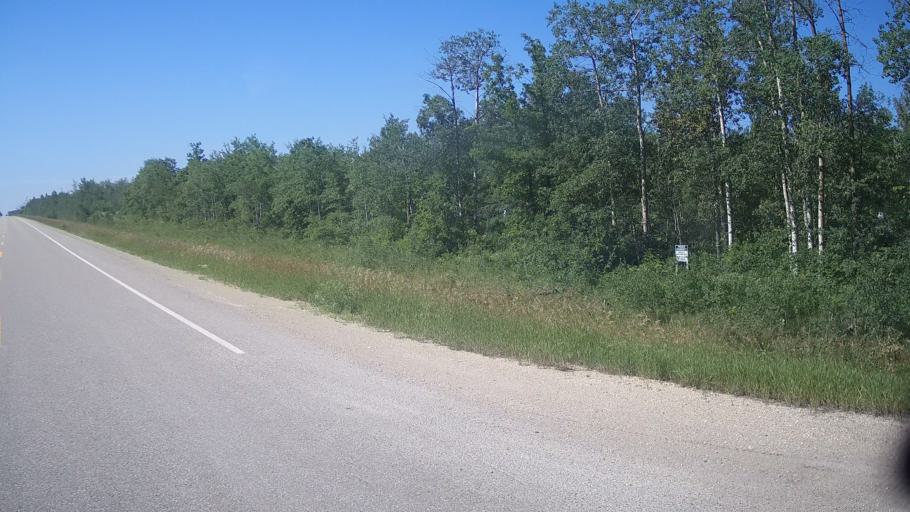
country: CA
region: Manitoba
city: La Broquerie
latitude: 49.6777
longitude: -96.4569
